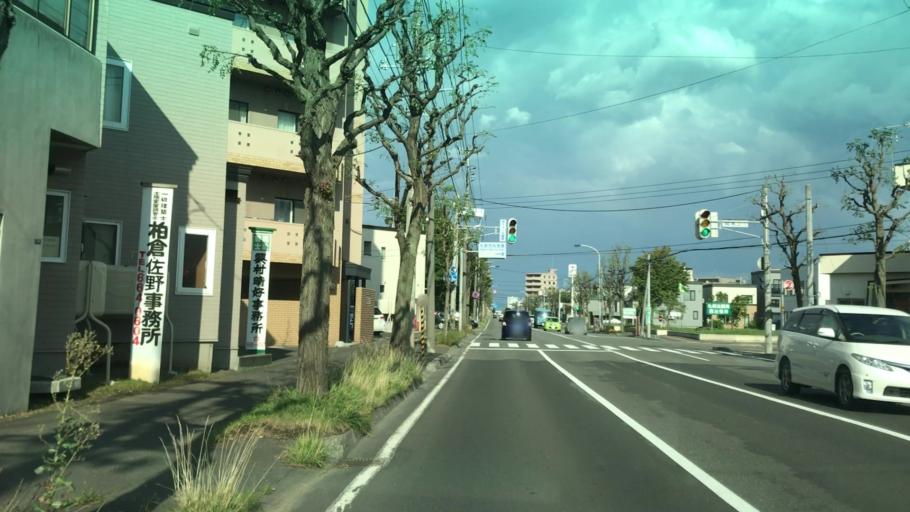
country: JP
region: Hokkaido
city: Sapporo
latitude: 43.0841
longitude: 141.2995
